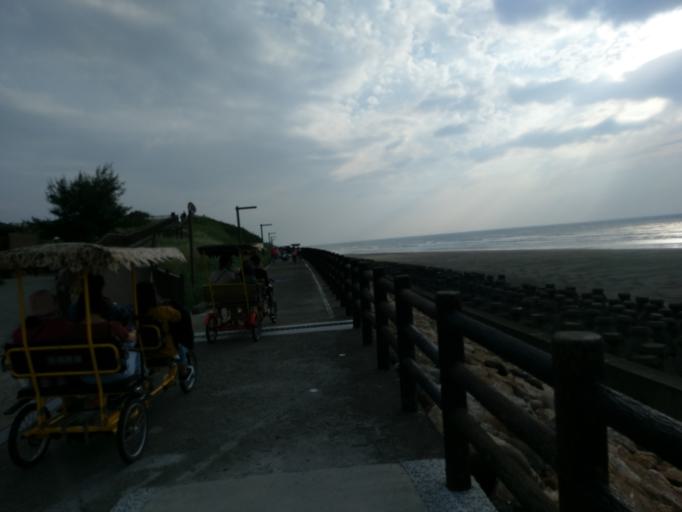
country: TW
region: Taiwan
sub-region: Hsinchu
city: Hsinchu
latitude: 24.8345
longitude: 120.9159
